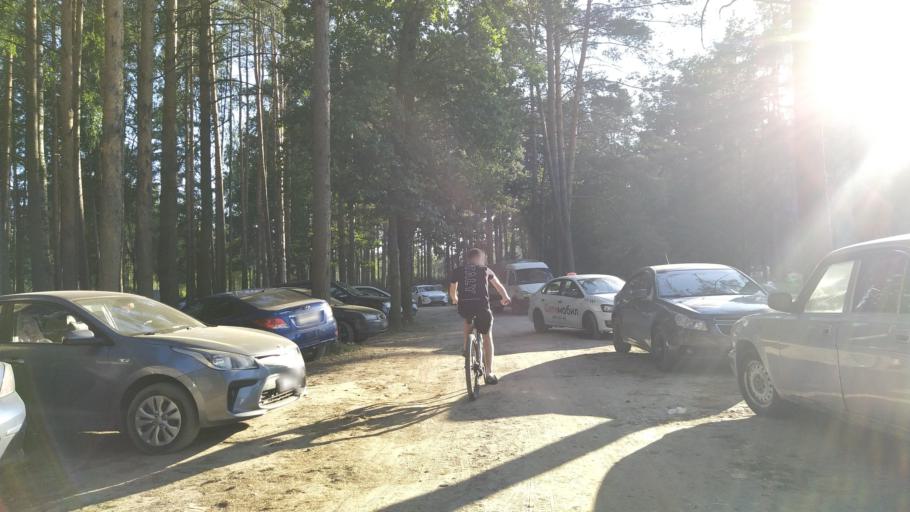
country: RU
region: Leningrad
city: Koltushi
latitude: 59.9191
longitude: 30.7365
